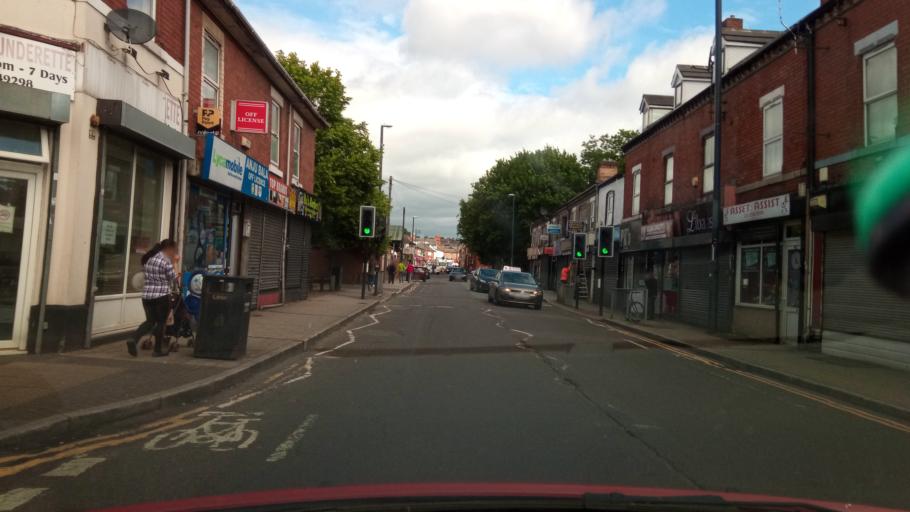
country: GB
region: England
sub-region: Derby
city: Derby
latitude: 52.9065
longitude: -1.4778
